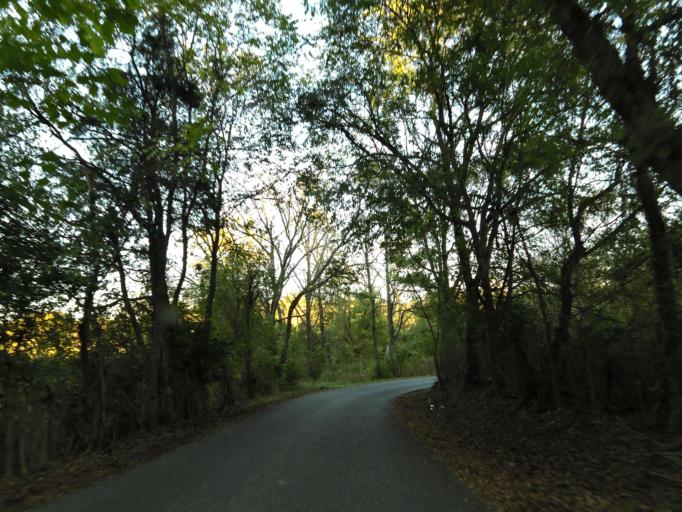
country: US
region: Tennessee
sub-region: Knox County
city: Knoxville
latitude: 36.0172
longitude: -83.9973
